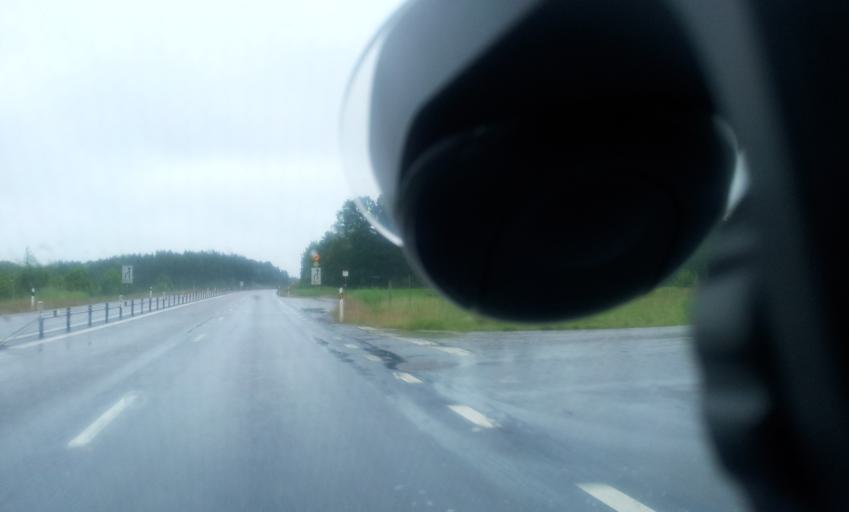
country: SE
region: OEstergoetland
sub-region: Valdemarsviks Kommun
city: Gusum
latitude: 58.3602
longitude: 16.4387
